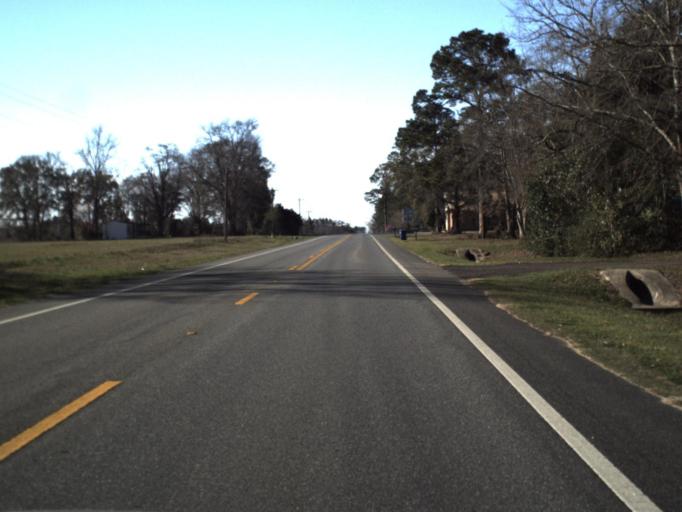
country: US
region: Florida
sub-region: Calhoun County
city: Blountstown
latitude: 30.4549
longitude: -85.1873
